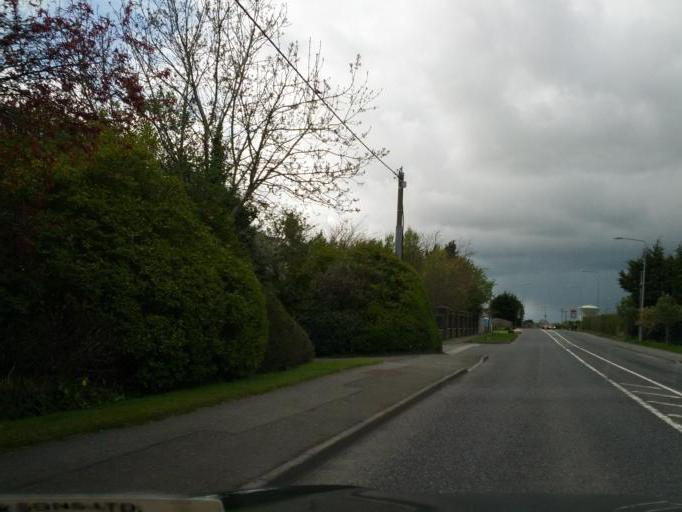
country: IE
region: Leinster
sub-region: An Mhi
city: Dunshaughlin
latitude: 53.5157
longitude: -6.5431
